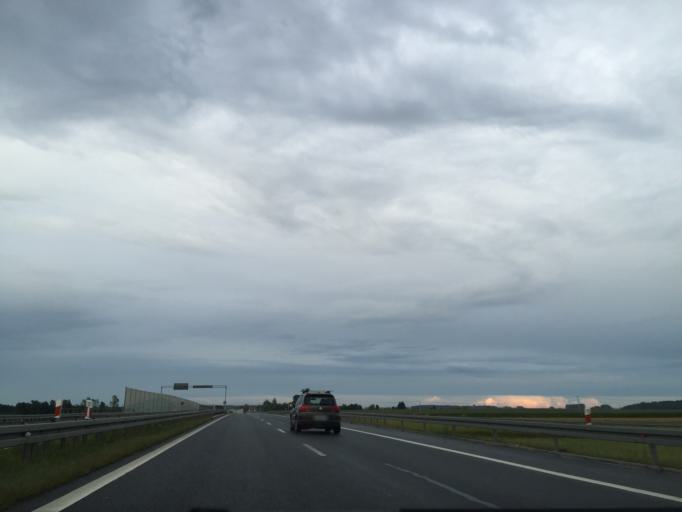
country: PL
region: Podlasie
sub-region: Powiat zambrowski
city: Zambrow
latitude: 53.0068
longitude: 22.2880
